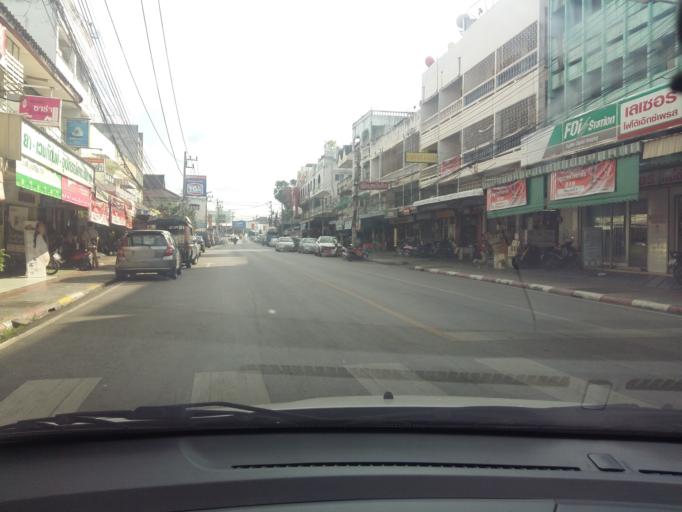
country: TH
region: Lampang
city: Lampang
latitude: 18.2839
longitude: 99.4995
